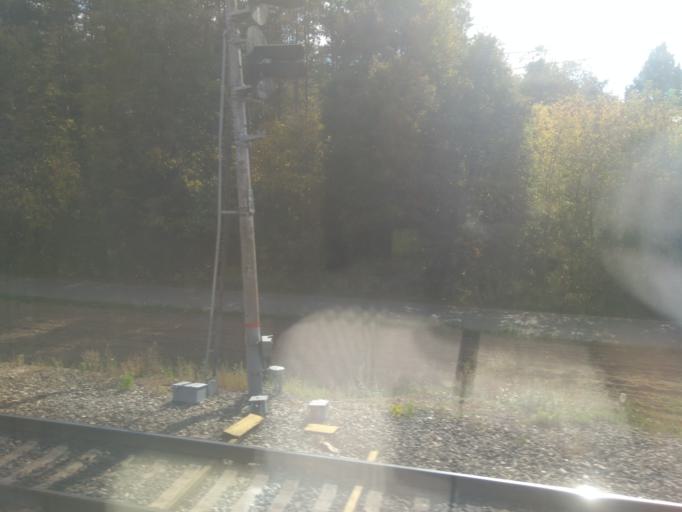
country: RU
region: Tatarstan
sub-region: Zelenodol'skiy Rayon
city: Zelenodolsk
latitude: 55.8417
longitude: 48.5776
